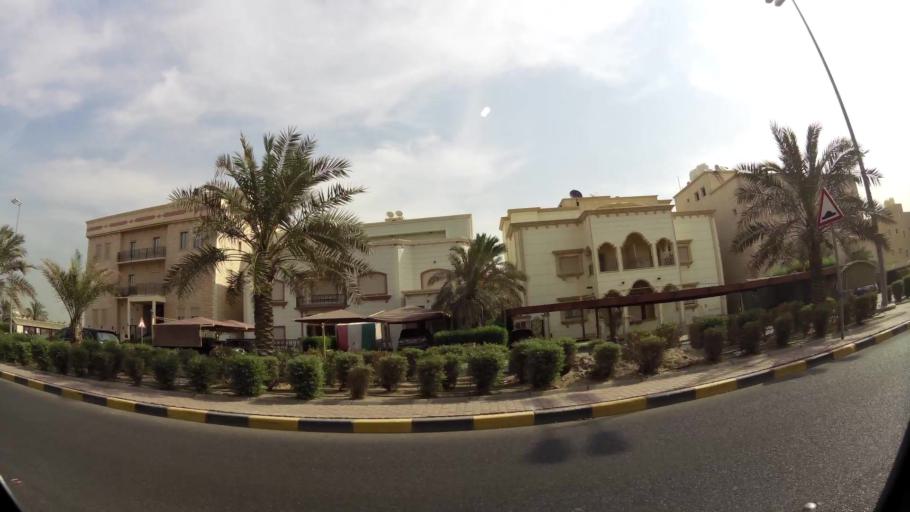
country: KW
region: Al Farwaniyah
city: Janub as Surrah
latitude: 29.2842
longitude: 47.9940
